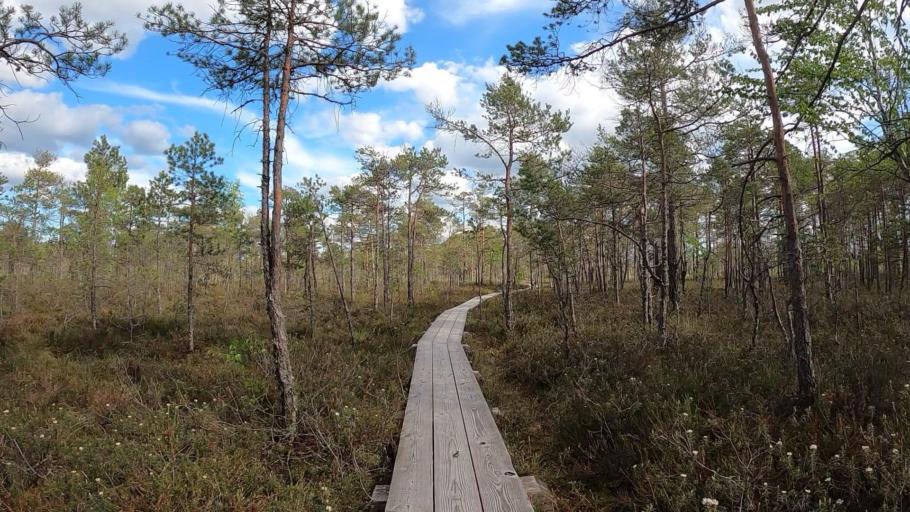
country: LV
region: Jurmala
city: Jurmala
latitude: 56.8527
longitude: 23.8138
